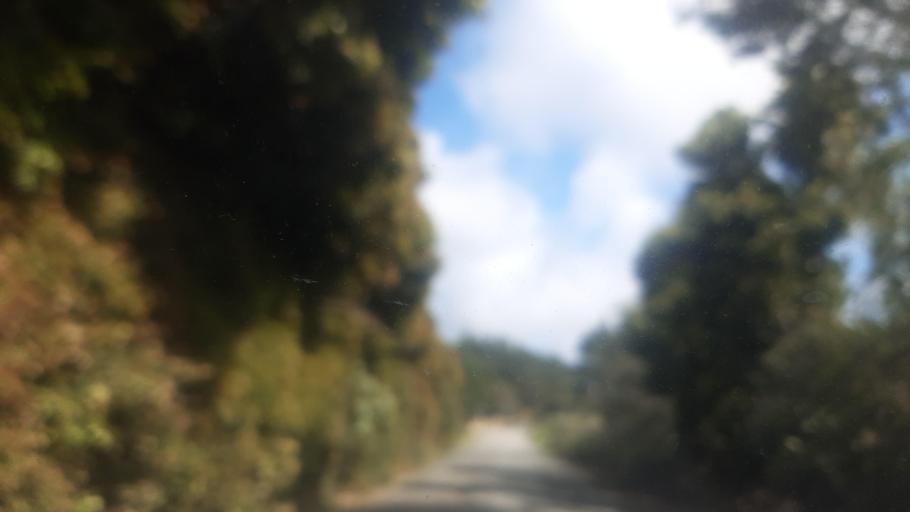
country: NZ
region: Northland
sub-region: Far North District
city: Kaitaia
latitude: -34.7669
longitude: 173.0469
